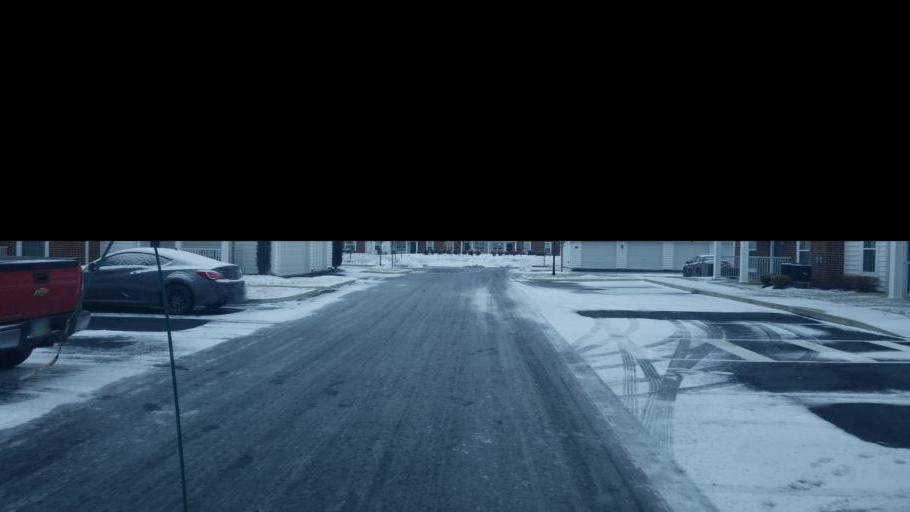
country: US
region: Ohio
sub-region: Franklin County
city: New Albany
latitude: 40.0589
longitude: -82.8460
